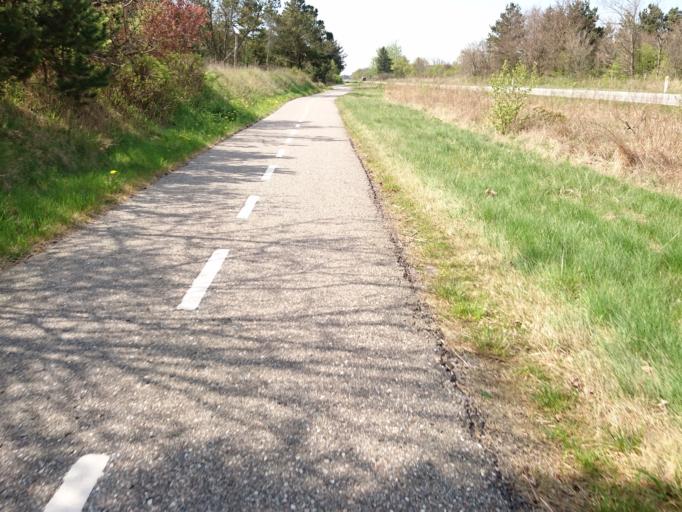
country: DK
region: North Denmark
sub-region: Frederikshavn Kommune
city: Strandby
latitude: 57.6198
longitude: 10.4386
